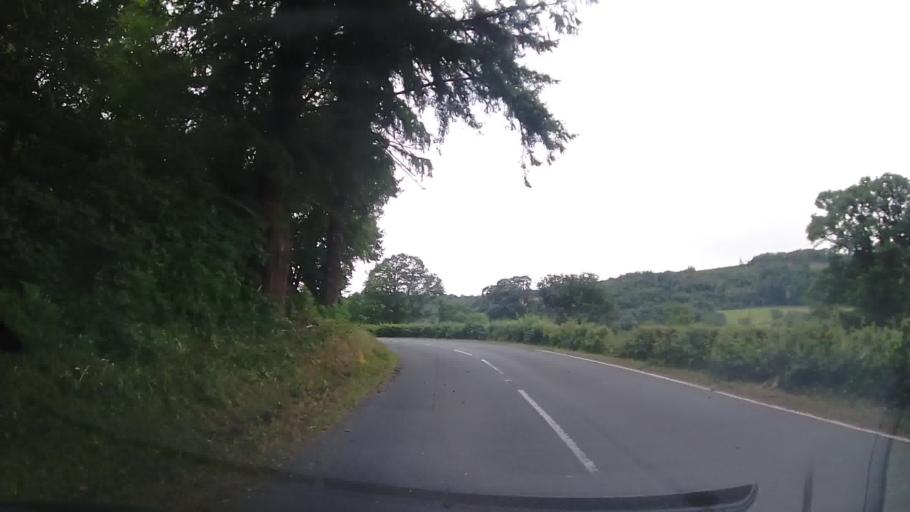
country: GB
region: Wales
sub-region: Denbighshire
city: Llandrillo
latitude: 52.9211
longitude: -3.4681
